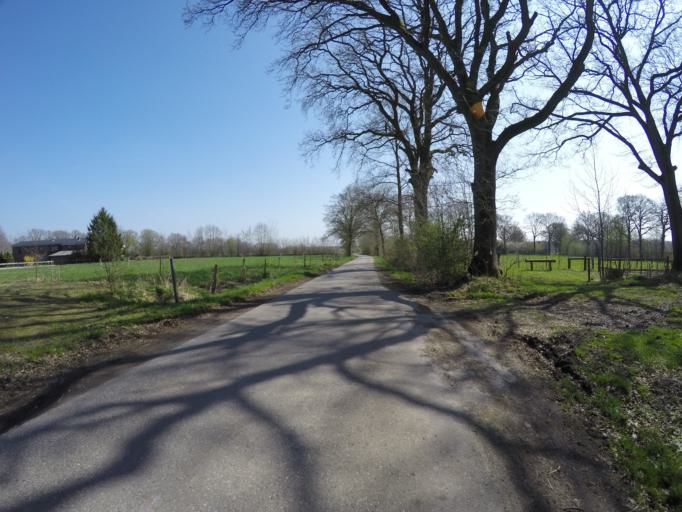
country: DE
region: Schleswig-Holstein
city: Hemdingen
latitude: 53.7588
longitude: 9.8496
